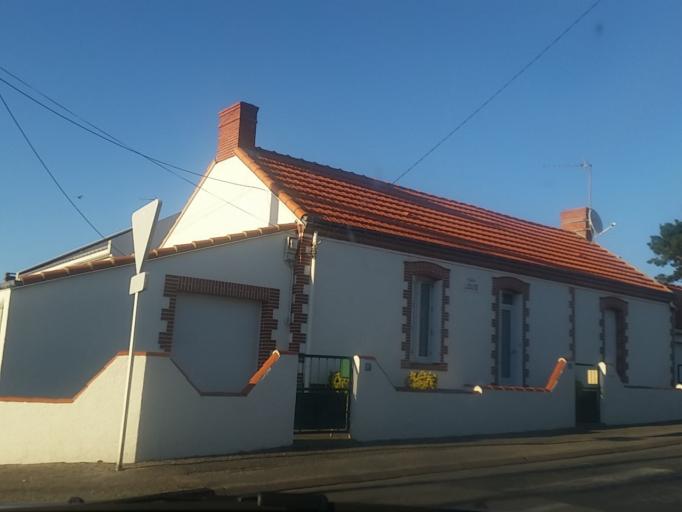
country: FR
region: Pays de la Loire
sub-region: Departement de la Loire-Atlantique
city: Saint-Michel-Chef-Chef
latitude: 47.1824
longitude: -2.1517
